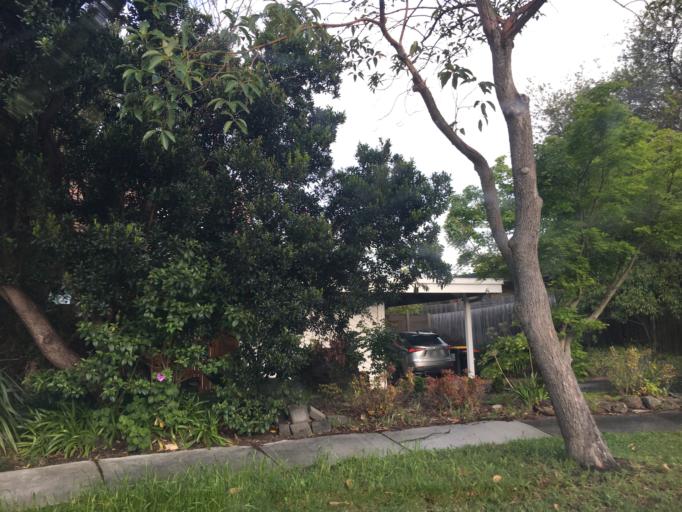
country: AU
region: Victoria
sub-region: Whitehorse
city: Vermont South
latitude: -37.8796
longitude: 145.1803
